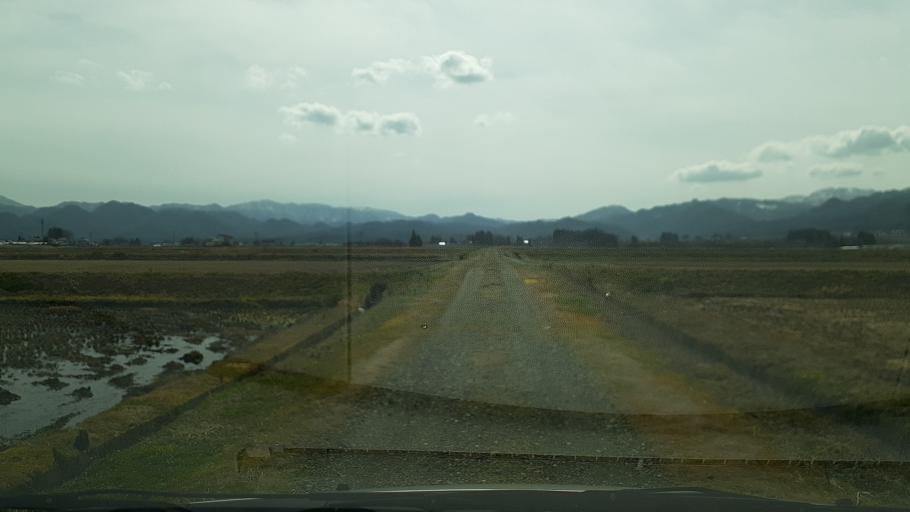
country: JP
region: Fukushima
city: Kitakata
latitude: 37.4659
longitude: 139.8284
